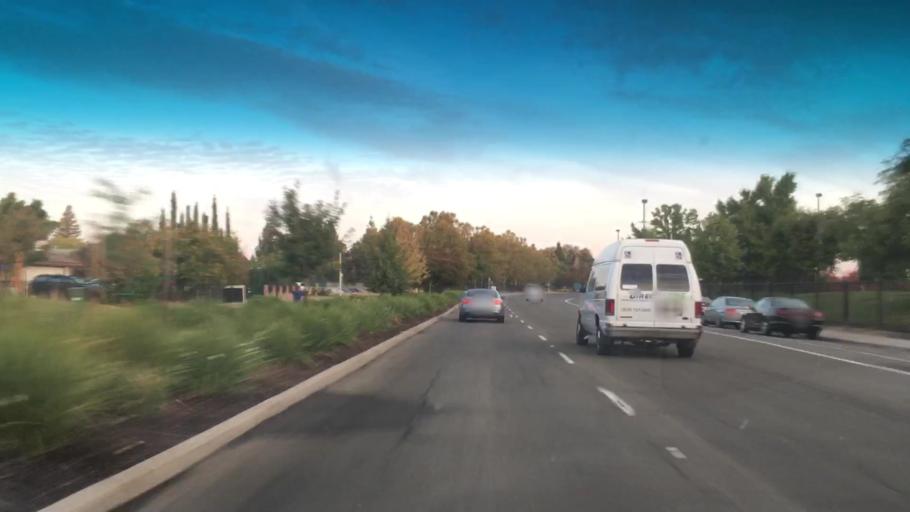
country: US
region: California
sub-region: Sacramento County
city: Laguna
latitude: 38.4516
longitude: -121.4268
